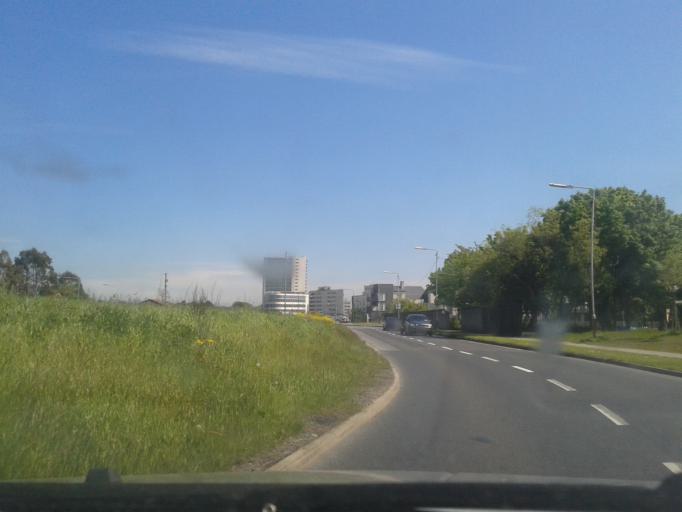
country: IE
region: Leinster
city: Ballymun
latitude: 53.4024
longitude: -6.2724
